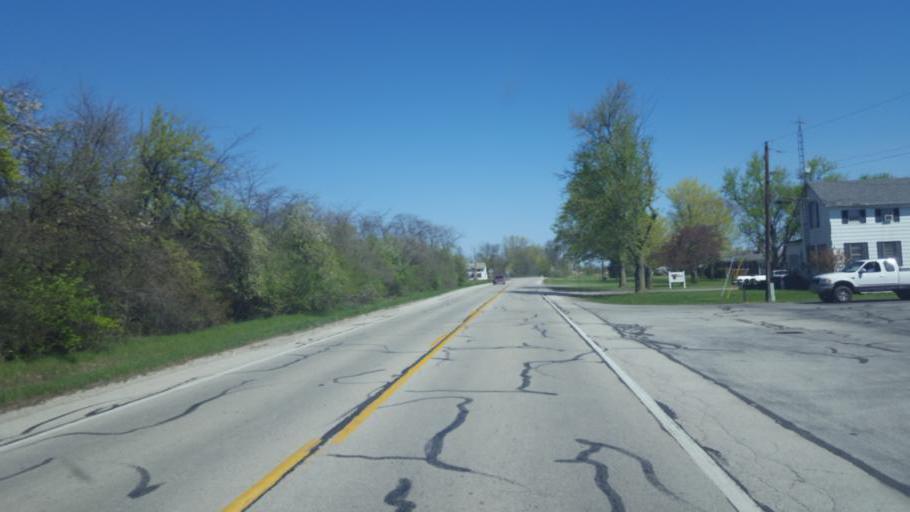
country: US
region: Ohio
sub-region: Sandusky County
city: Fremont
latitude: 41.3769
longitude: -83.1348
